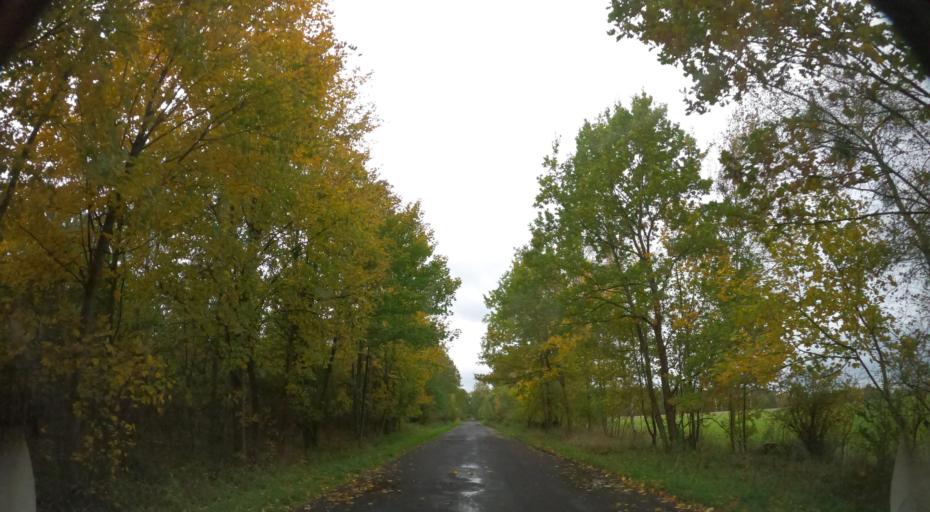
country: PL
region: West Pomeranian Voivodeship
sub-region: Powiat goleniowski
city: Stepnica
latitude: 53.6664
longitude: 14.6654
